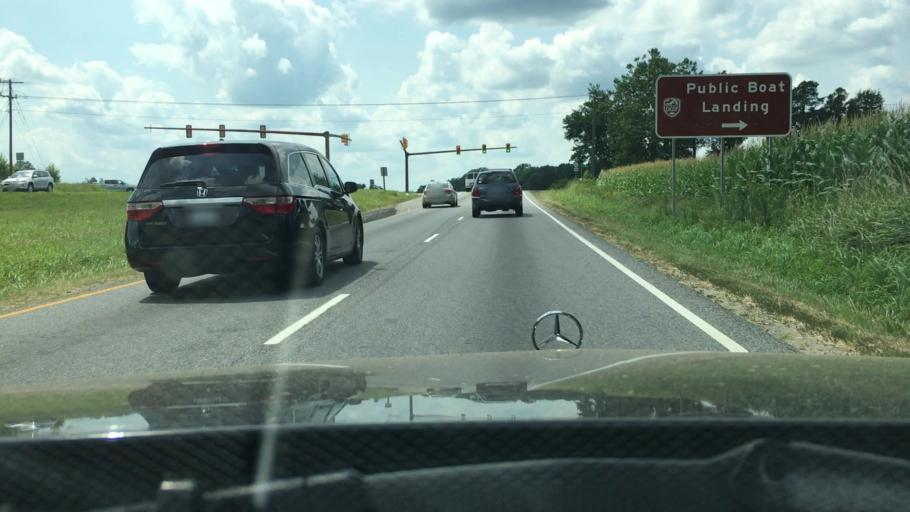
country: US
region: Virginia
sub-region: Spotsylvania County
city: Spotsylvania
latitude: 38.3080
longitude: -77.6330
